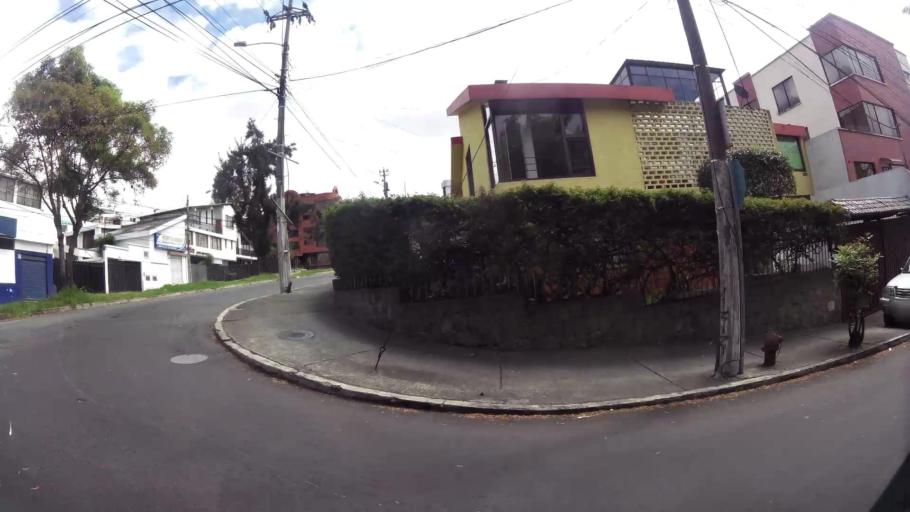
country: EC
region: Pichincha
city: Quito
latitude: -0.1565
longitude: -78.4918
